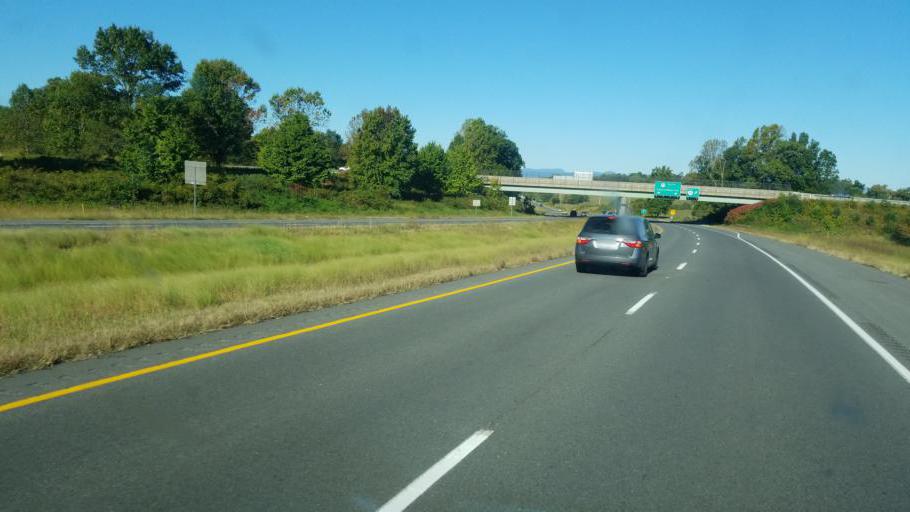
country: US
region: Virginia
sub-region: Culpeper County
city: Culpeper
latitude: 38.4531
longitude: -78.0211
